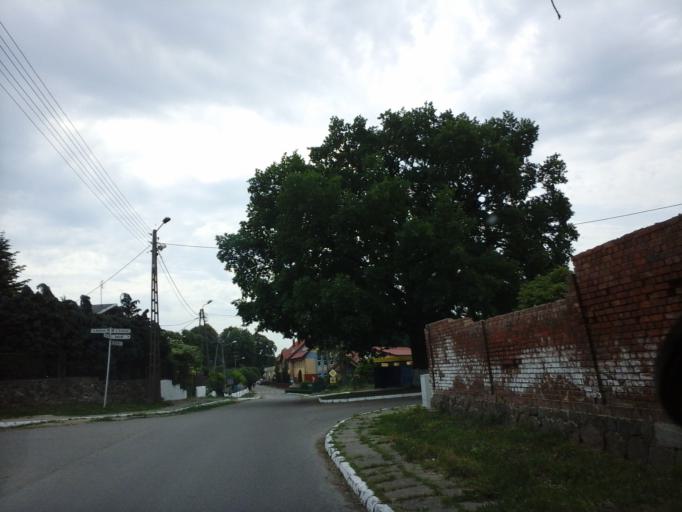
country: PL
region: West Pomeranian Voivodeship
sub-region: Powiat choszczenski
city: Krzecin
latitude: 53.1460
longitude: 15.5491
